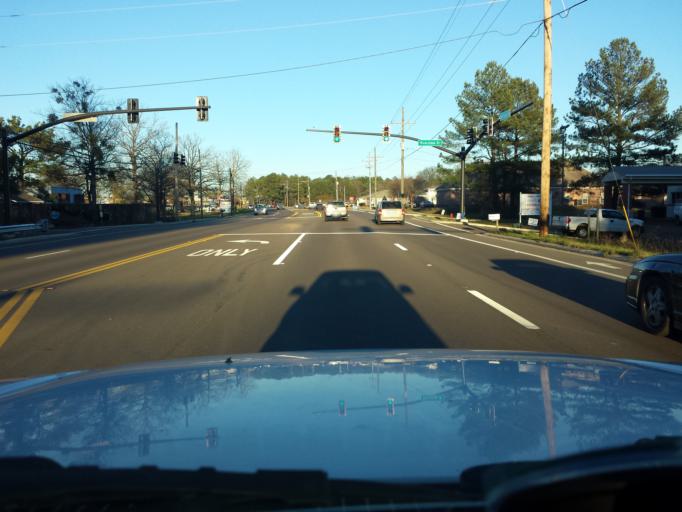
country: US
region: Mississippi
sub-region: Madison County
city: Ridgeland
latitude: 32.3744
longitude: -90.0476
